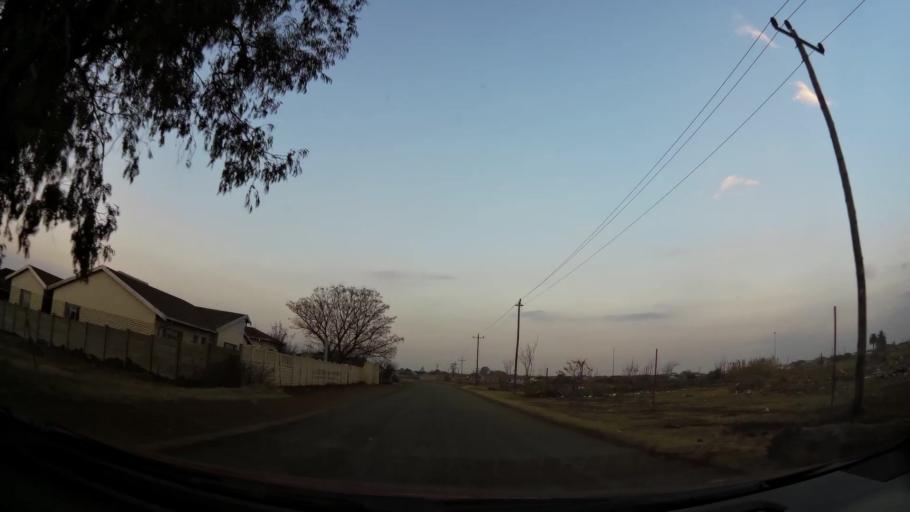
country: ZA
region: Gauteng
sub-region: City of Johannesburg Metropolitan Municipality
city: Orange Farm
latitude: -26.5461
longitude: 27.8774
